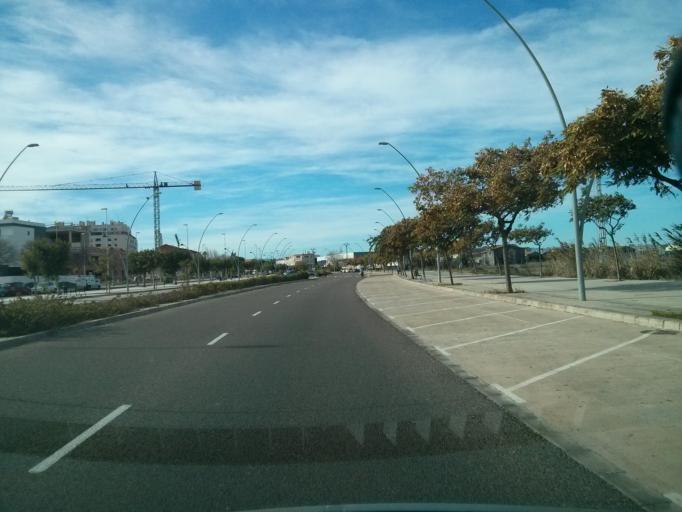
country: ES
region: Valencia
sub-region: Provincia de Castello
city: Castello de la Plana
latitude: 39.9997
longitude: -0.0341
